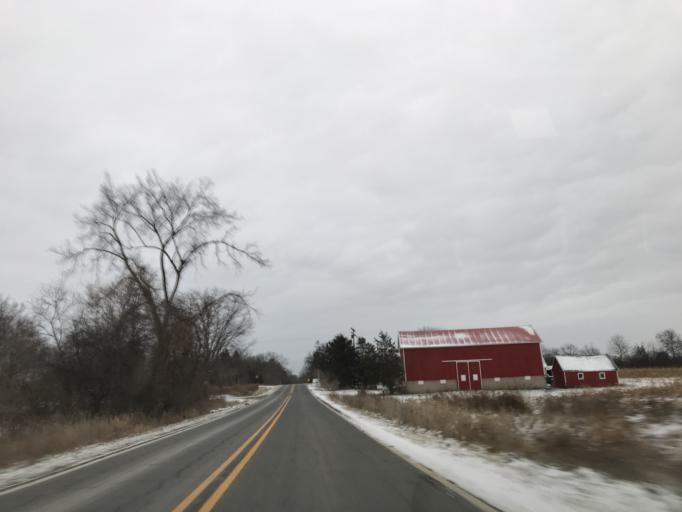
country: US
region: Michigan
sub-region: Washtenaw County
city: Ann Arbor
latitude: 42.3439
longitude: -83.7064
